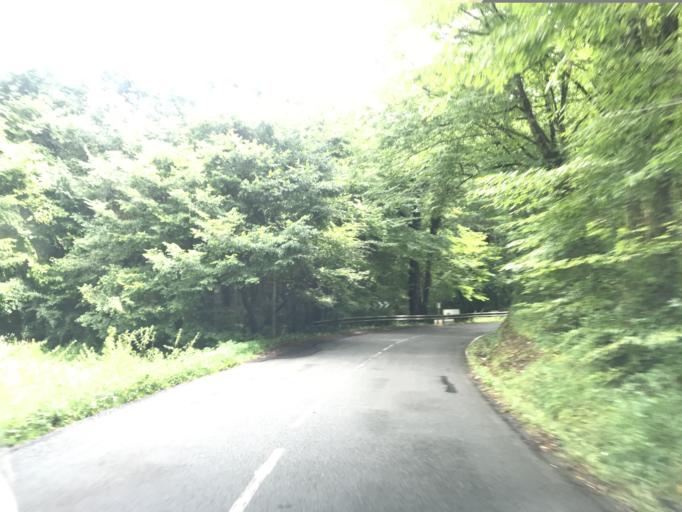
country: FR
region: Aquitaine
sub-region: Departement de la Dordogne
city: Chancelade
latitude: 45.1763
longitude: 0.6779
